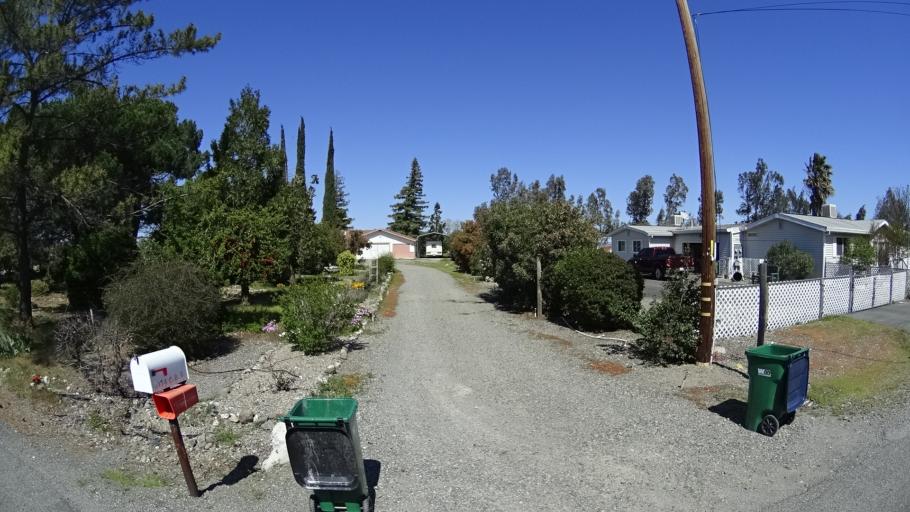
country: US
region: California
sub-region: Glenn County
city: Orland
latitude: 39.7769
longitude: -122.2332
